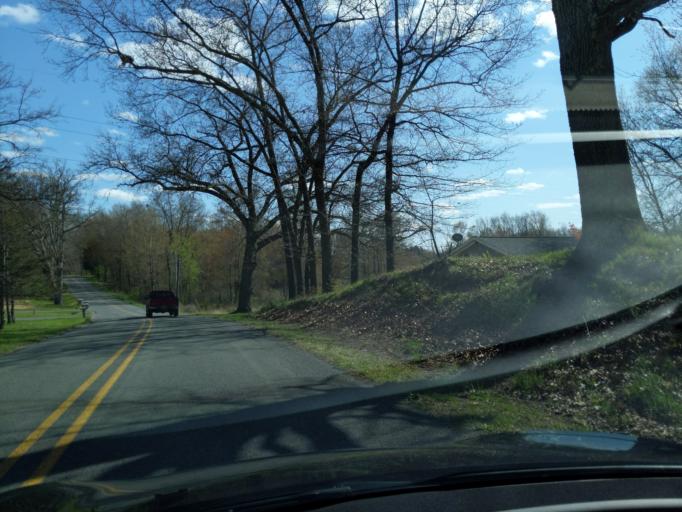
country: US
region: Michigan
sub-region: Jackson County
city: Spring Arbor
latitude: 42.3283
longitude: -84.5213
